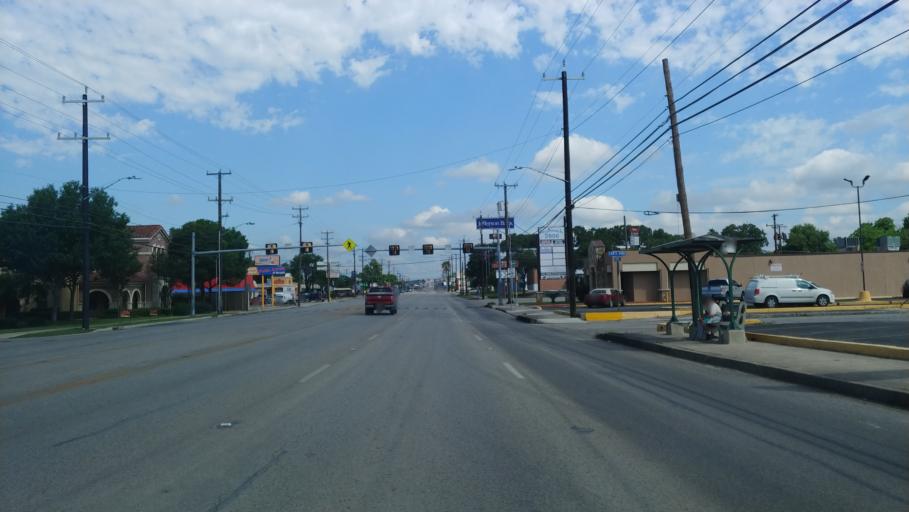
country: US
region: Texas
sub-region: Bexar County
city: Balcones Heights
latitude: 29.4693
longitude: -98.5308
